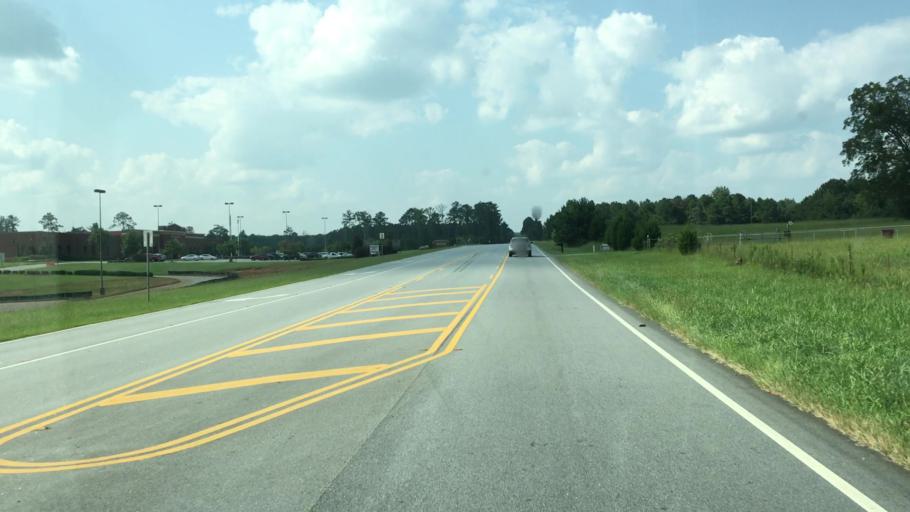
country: US
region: Georgia
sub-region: Jasper County
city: Monticello
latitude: 33.3349
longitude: -83.7119
